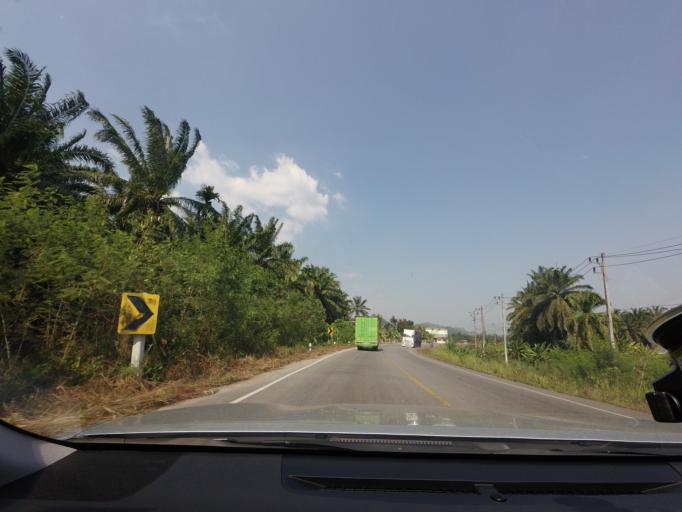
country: TH
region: Krabi
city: Plai Phraya
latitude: 8.5572
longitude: 98.7938
